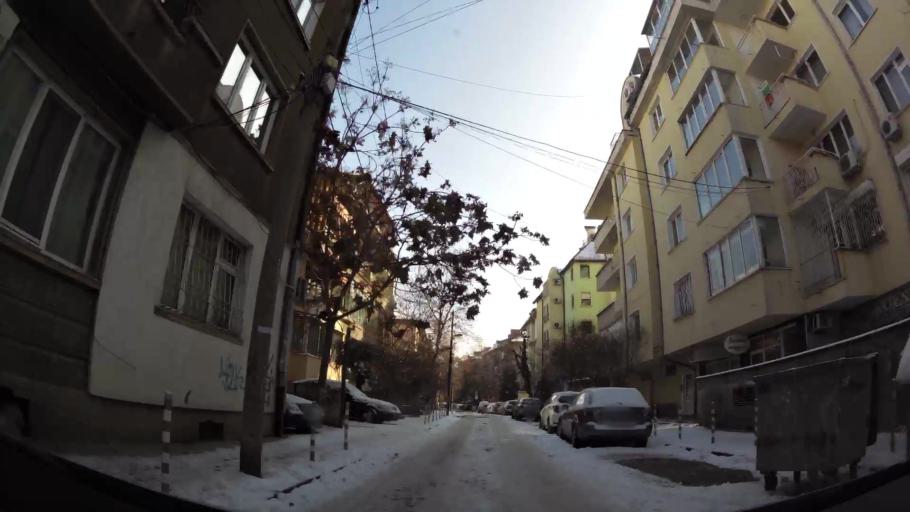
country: BG
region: Sofia-Capital
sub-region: Stolichna Obshtina
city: Sofia
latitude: 42.6815
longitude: 23.3271
